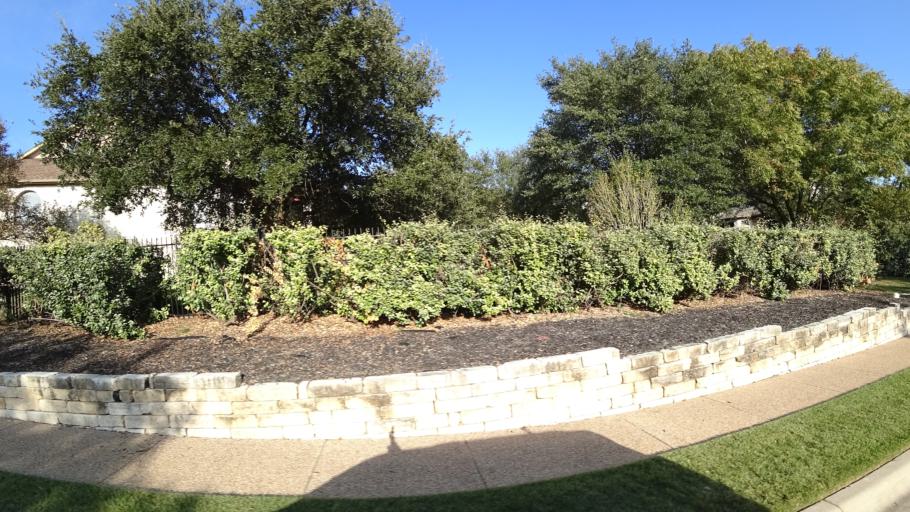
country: US
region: Texas
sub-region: Williamson County
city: Anderson Mill
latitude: 30.4280
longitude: -97.8075
